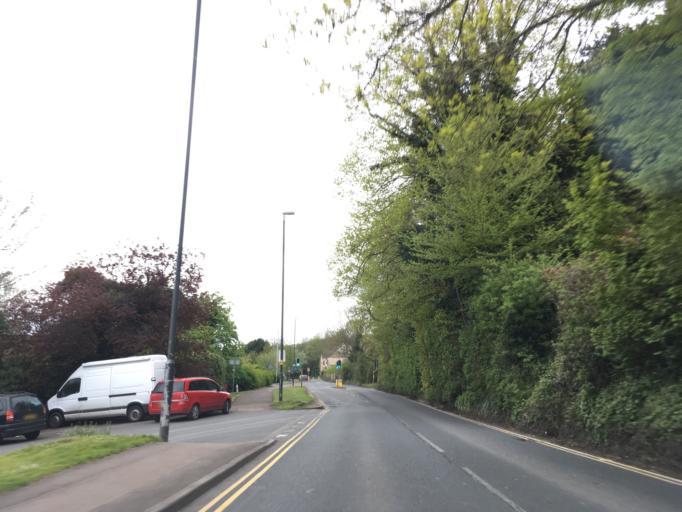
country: GB
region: England
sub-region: Gloucestershire
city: Stroud
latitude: 51.7380
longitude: -2.2359
